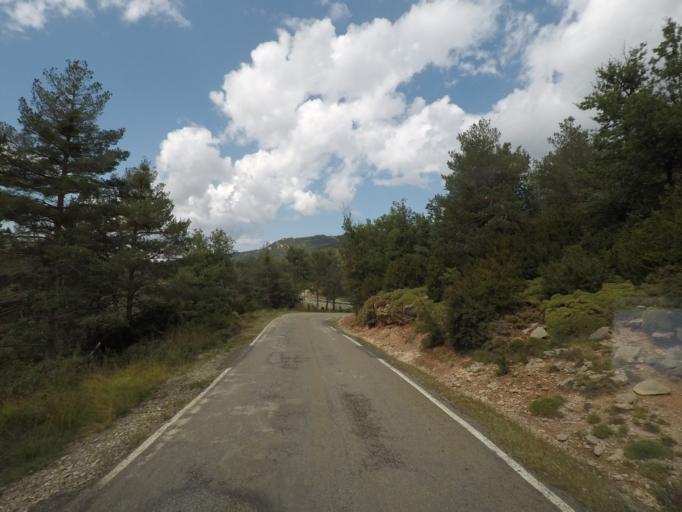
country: ES
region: Aragon
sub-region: Provincia de Huesca
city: Boltana
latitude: 42.3976
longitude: -0.0435
